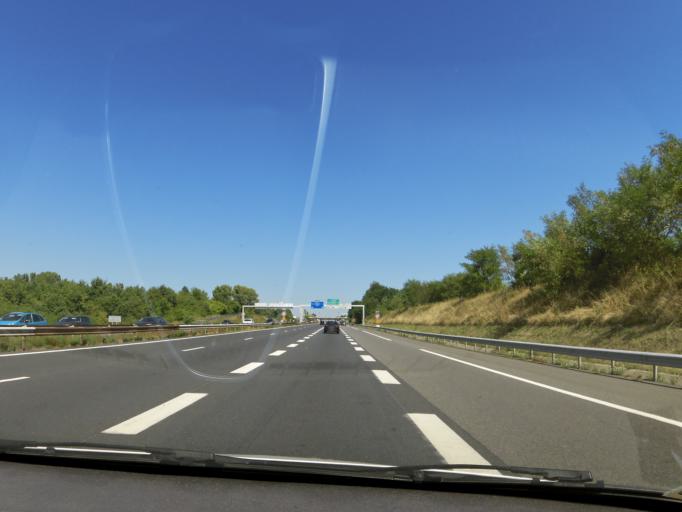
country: FR
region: Rhone-Alpes
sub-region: Departement du Rhone
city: Dardilly
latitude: 45.8145
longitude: 4.7672
